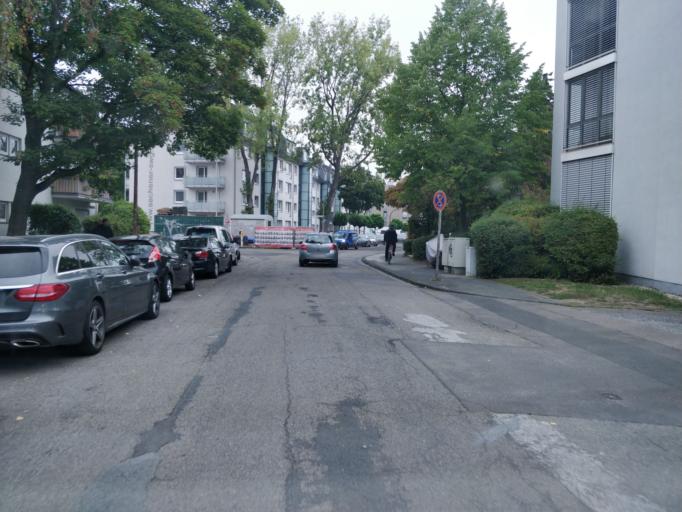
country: DE
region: North Rhine-Westphalia
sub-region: Regierungsbezirk Koln
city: Mengenich
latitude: 50.9394
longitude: 6.8924
